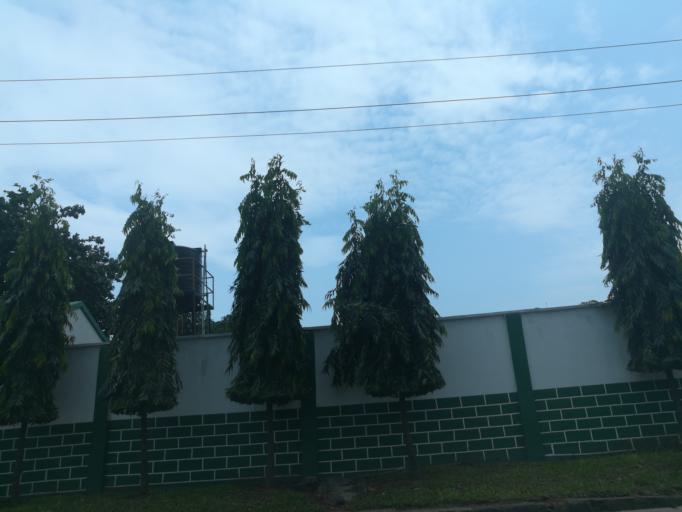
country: NG
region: Lagos
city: Ikeja
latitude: 6.6078
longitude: 3.3617
